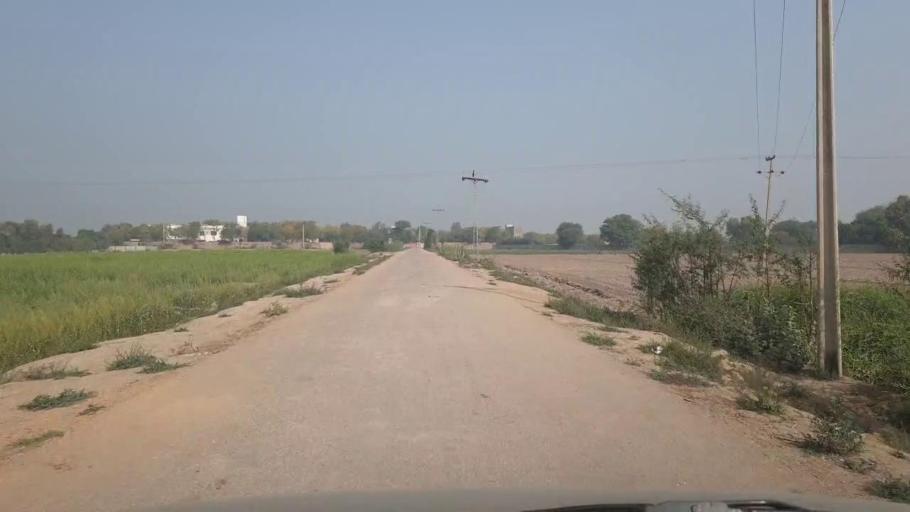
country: PK
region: Sindh
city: Umarkot
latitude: 25.3738
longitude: 69.7383
